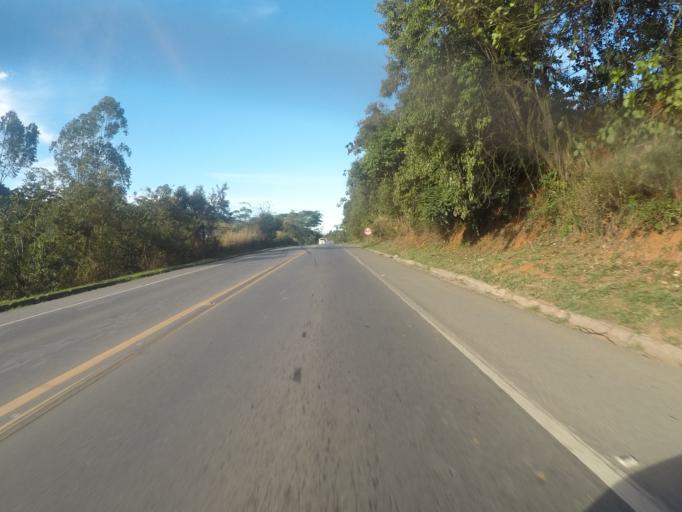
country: BR
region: Espirito Santo
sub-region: Ibiracu
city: Ibiracu
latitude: -19.8678
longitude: -40.4041
